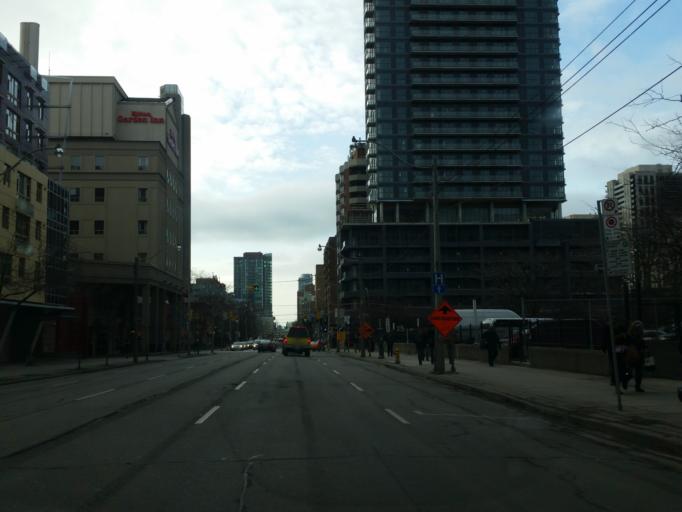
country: CA
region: Ontario
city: Toronto
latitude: 43.6580
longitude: -79.3750
